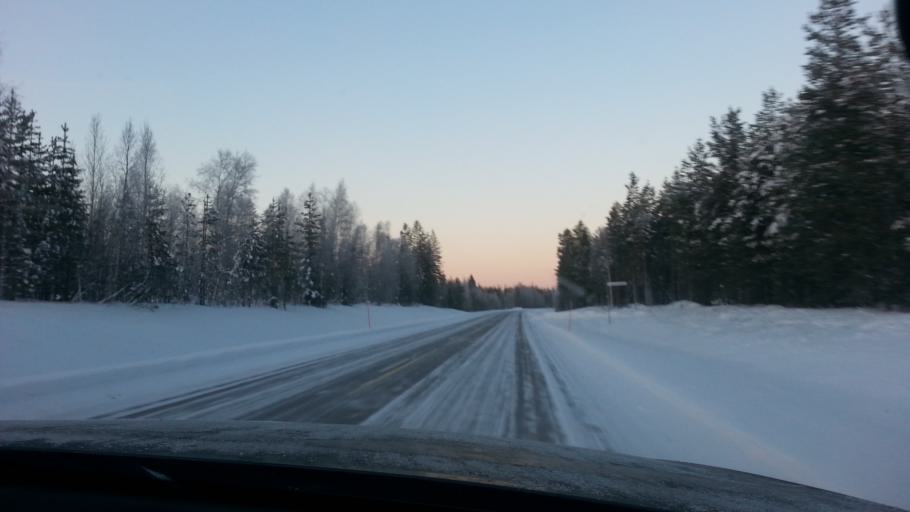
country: FI
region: Lapland
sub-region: Rovaniemi
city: Rovaniemi
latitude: 66.7779
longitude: 25.4524
